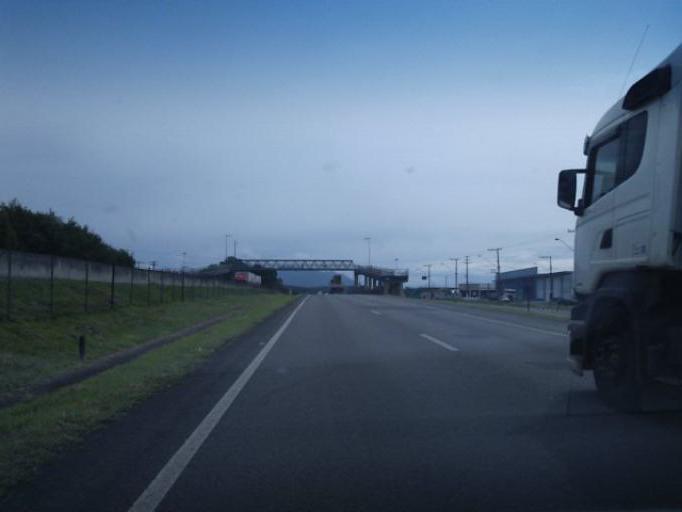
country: BR
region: Sao Paulo
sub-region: Jacupiranga
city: Jacupiranga
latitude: -24.7008
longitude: -48.0067
